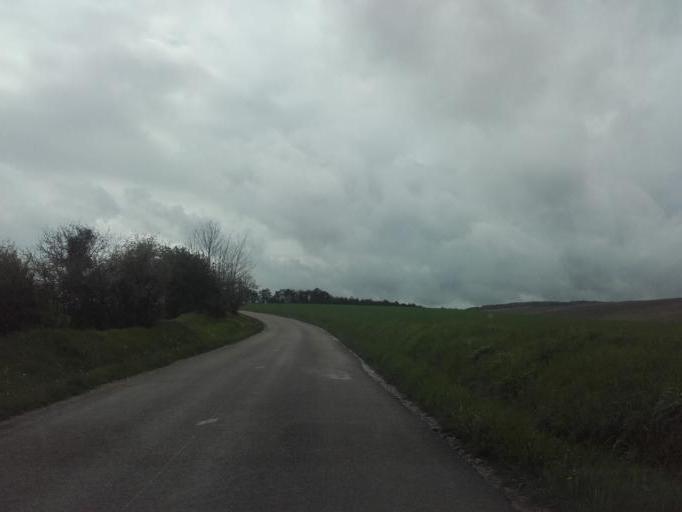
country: FR
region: Bourgogne
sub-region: Departement de l'Yonne
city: Chablis
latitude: 47.8011
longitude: 3.7954
